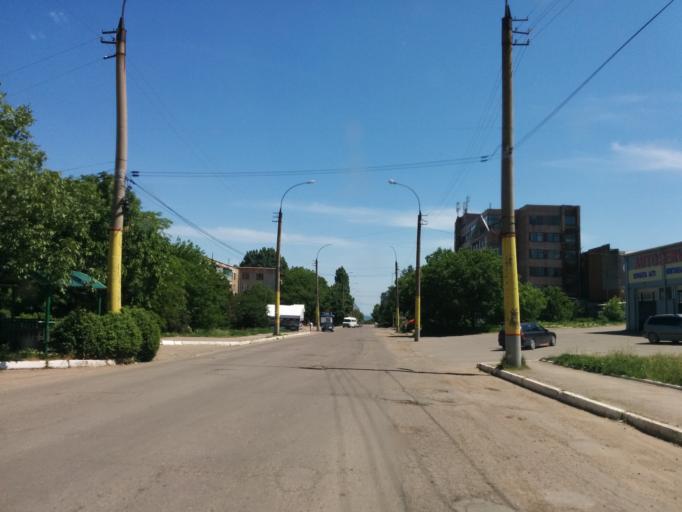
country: MD
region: Raionul Soroca
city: Soroca
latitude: 48.1627
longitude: 28.2676
